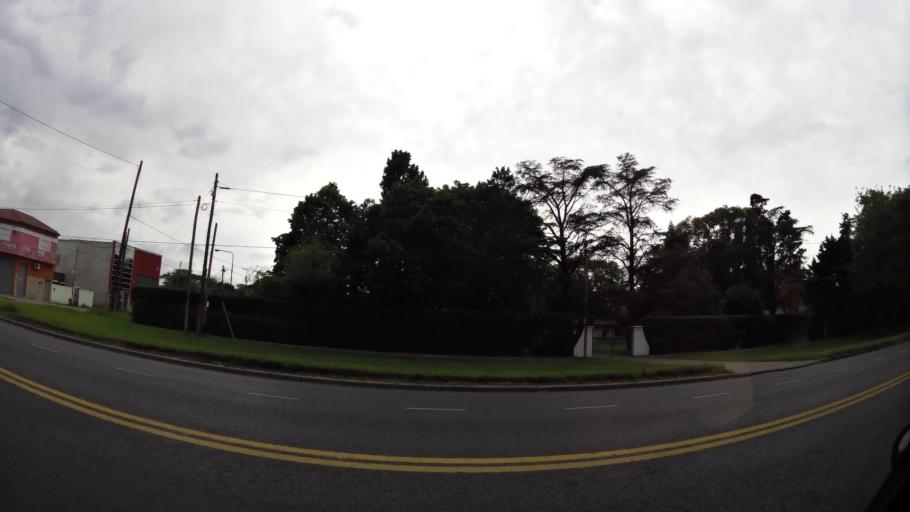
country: AR
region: Buenos Aires
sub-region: Partido de Quilmes
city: Quilmes
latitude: -34.7664
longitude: -58.2846
